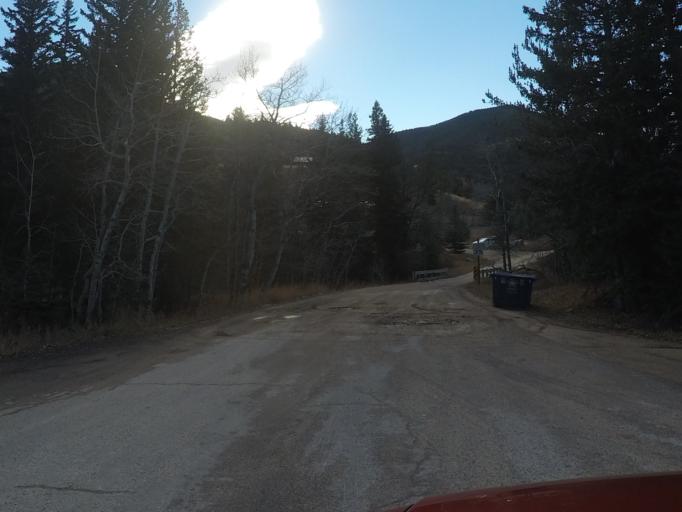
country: US
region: Montana
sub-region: Carbon County
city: Red Lodge
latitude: 45.1211
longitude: -109.2968
